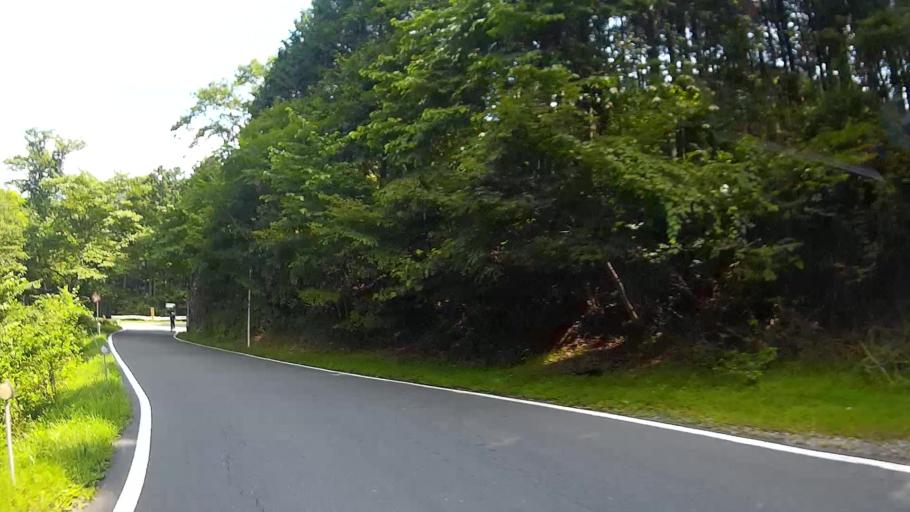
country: JP
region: Saitama
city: Chichibu
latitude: 35.9348
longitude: 139.1540
